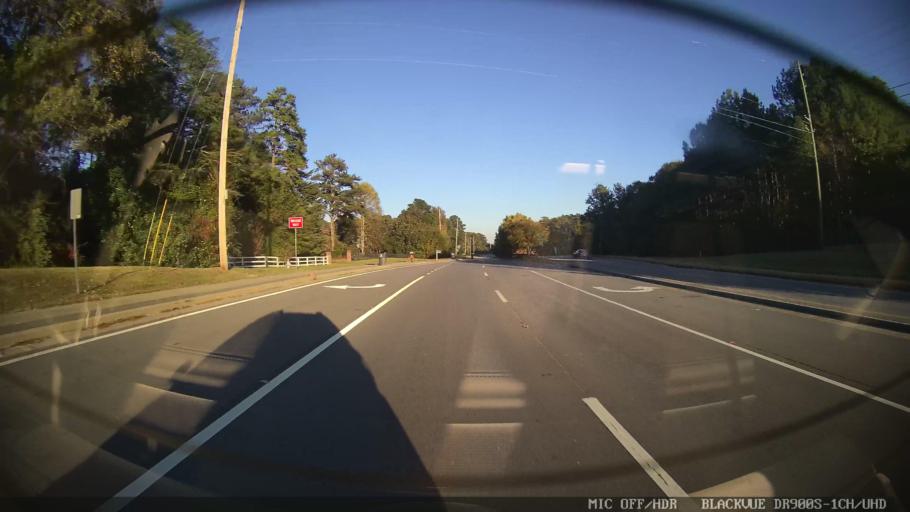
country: US
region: Georgia
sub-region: Clayton County
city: Morrow
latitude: 33.5411
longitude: -84.2961
